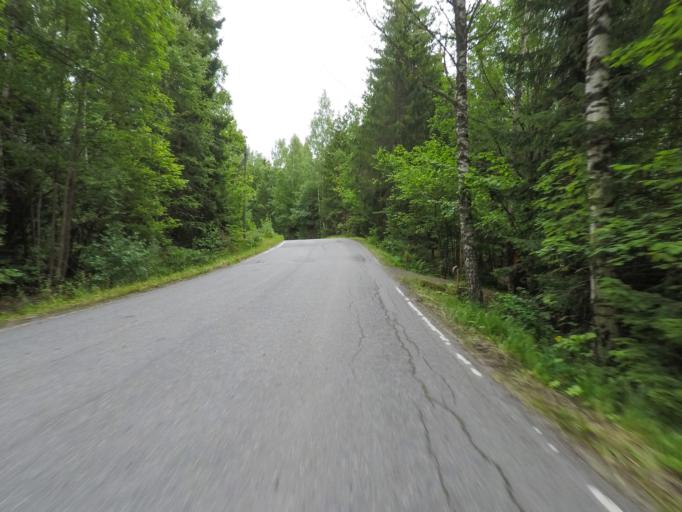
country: FI
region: Uusimaa
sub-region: Helsinki
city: Karjalohja
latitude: 60.2610
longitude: 23.7246
